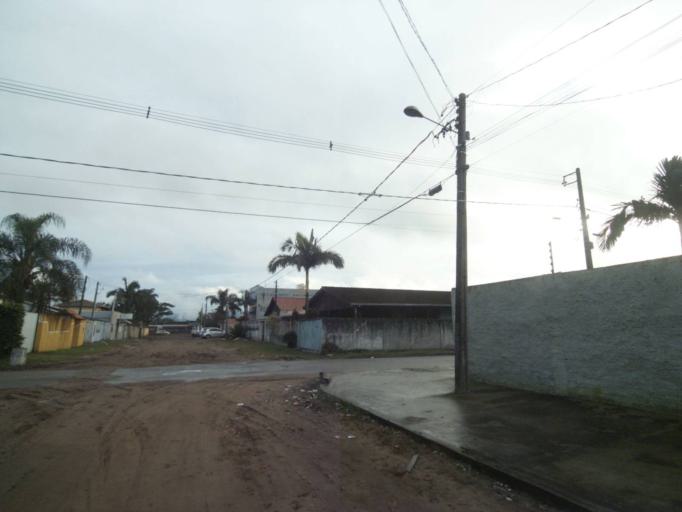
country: BR
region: Parana
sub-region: Paranagua
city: Paranagua
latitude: -25.5730
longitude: -48.5734
